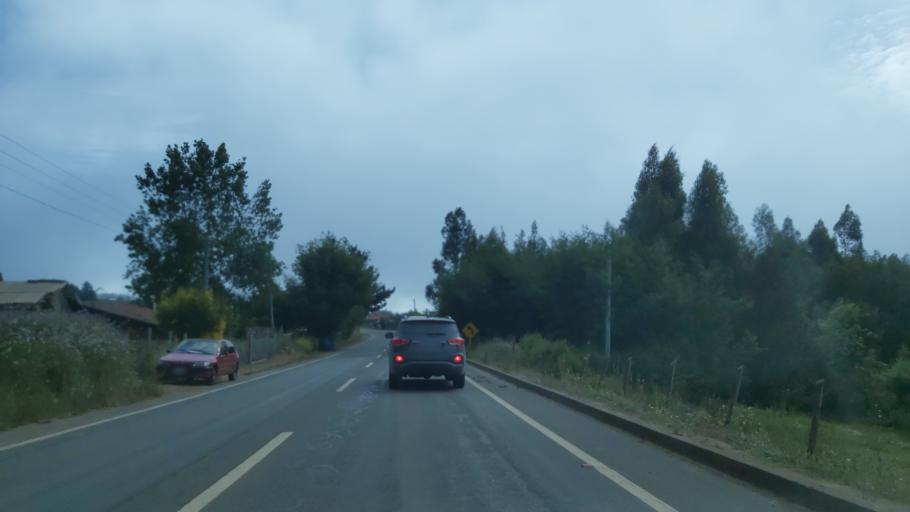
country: CL
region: Maule
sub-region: Provincia de Cauquenes
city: Cauquenes
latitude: -35.8706
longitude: -72.6572
